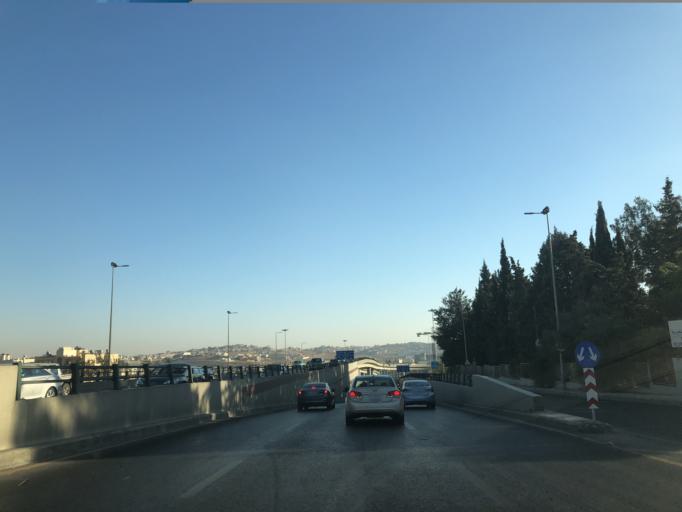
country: JO
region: Amman
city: Wadi as Sir
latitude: 31.9482
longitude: 35.8507
